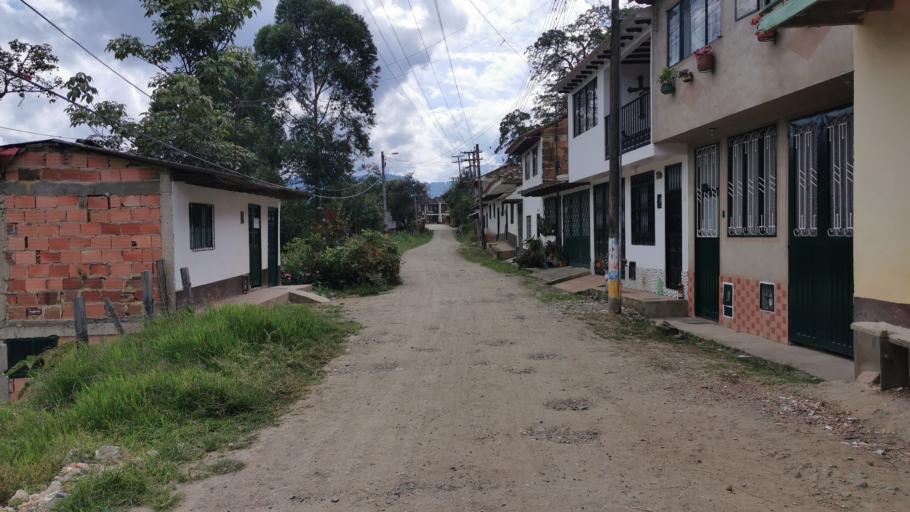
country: CO
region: Cundinamarca
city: Tenza
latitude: 5.0778
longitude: -73.4198
